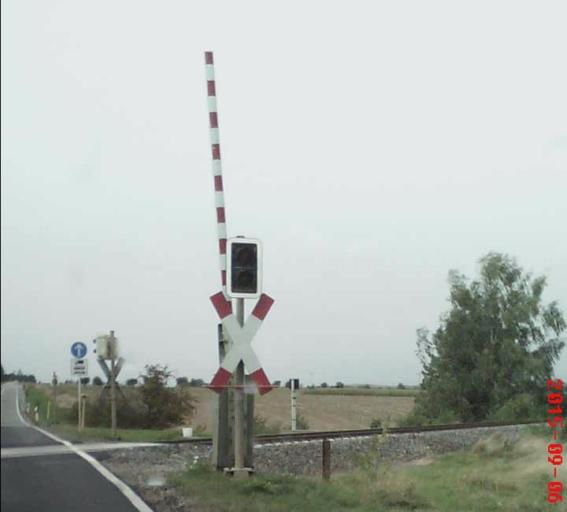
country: DE
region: Thuringia
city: Seebach
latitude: 51.1713
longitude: 10.5221
